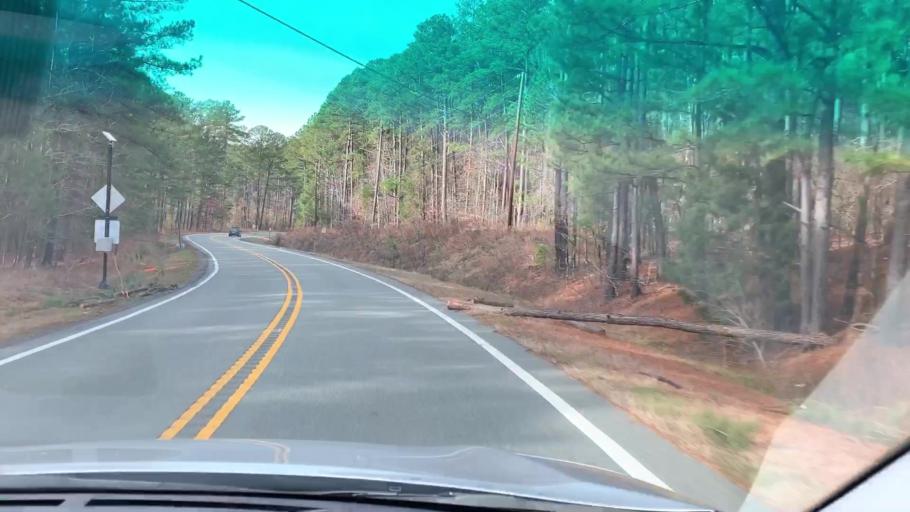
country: US
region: North Carolina
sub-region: Wake County
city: Green Level
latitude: 35.8470
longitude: -78.9267
